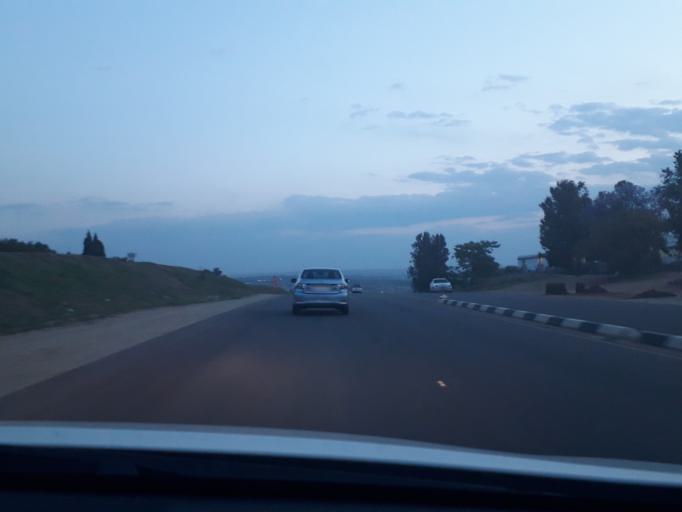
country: ZA
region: Gauteng
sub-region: City of Johannesburg Metropolitan Municipality
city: Midrand
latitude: -25.9863
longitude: 28.0767
